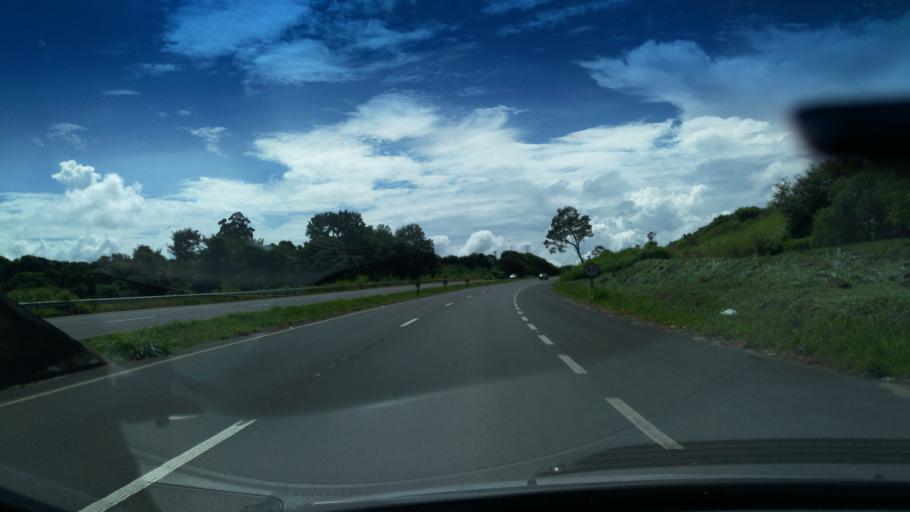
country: BR
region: Sao Paulo
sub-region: Santo Antonio Do Jardim
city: Espirito Santo do Pinhal
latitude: -22.1846
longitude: -46.7636
